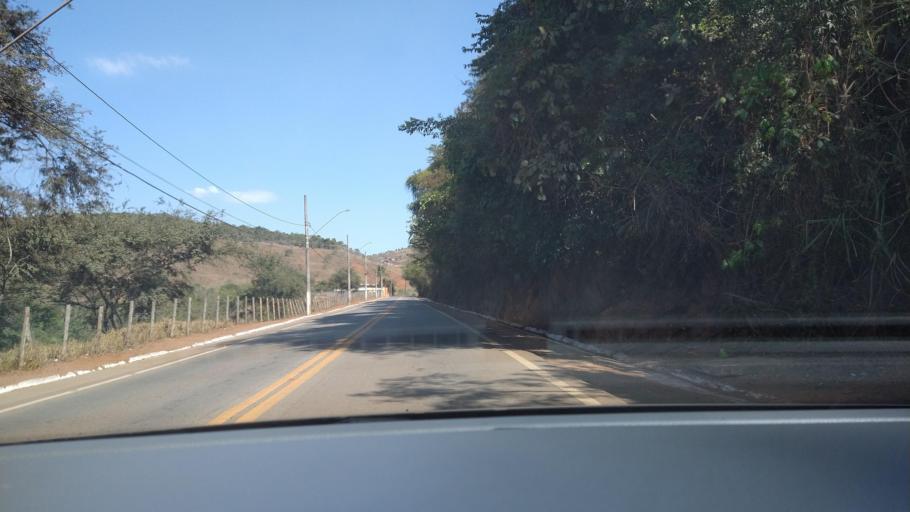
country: BR
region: Minas Gerais
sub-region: Rio Piracicaba
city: Rio Piracicaba
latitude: -19.9225
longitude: -43.1634
